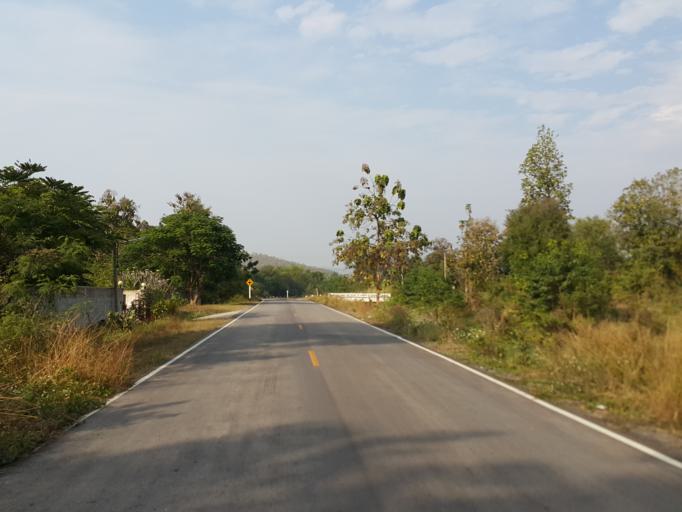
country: TH
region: Chiang Mai
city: San Sai
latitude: 18.8520
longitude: 99.1466
